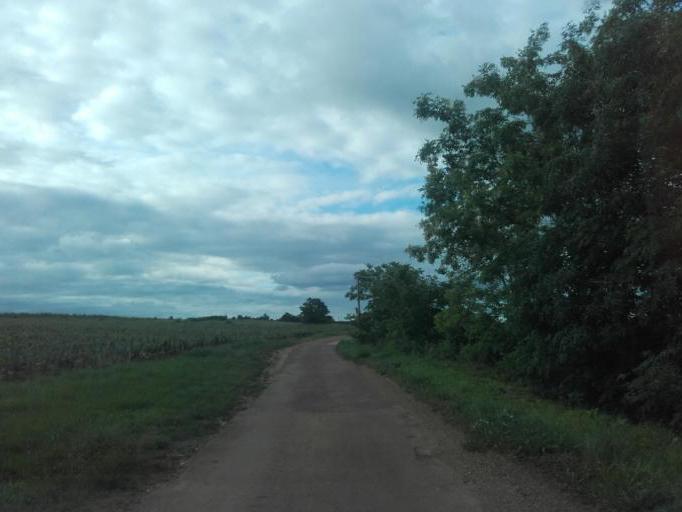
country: FR
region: Bourgogne
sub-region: Departement de Saone-et-Loire
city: Rully
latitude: 46.8599
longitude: 4.7403
